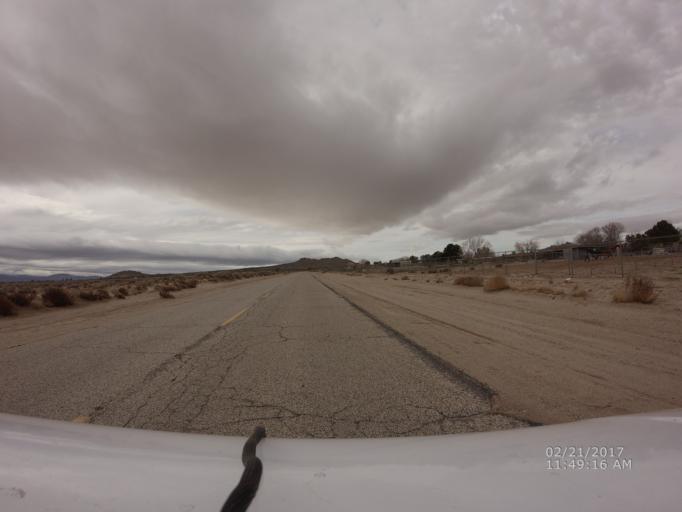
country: US
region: California
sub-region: Los Angeles County
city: Lake Los Angeles
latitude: 34.6312
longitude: -117.8559
